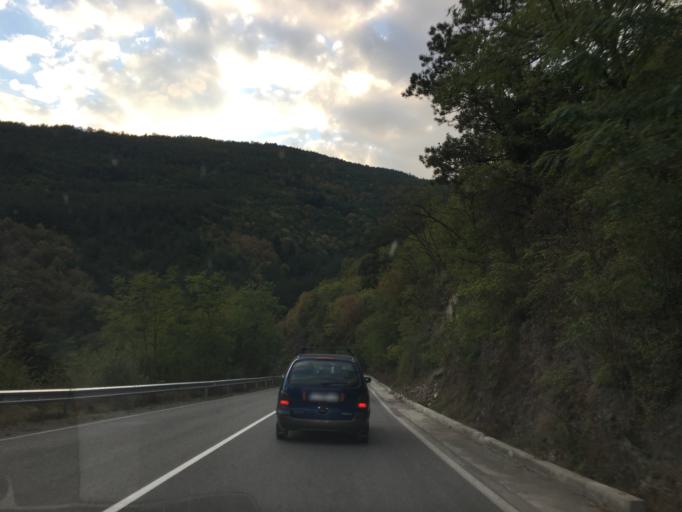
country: BG
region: Sofiya
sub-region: Obshtina Svoge
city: Svoge
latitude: 42.8805
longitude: 23.3776
